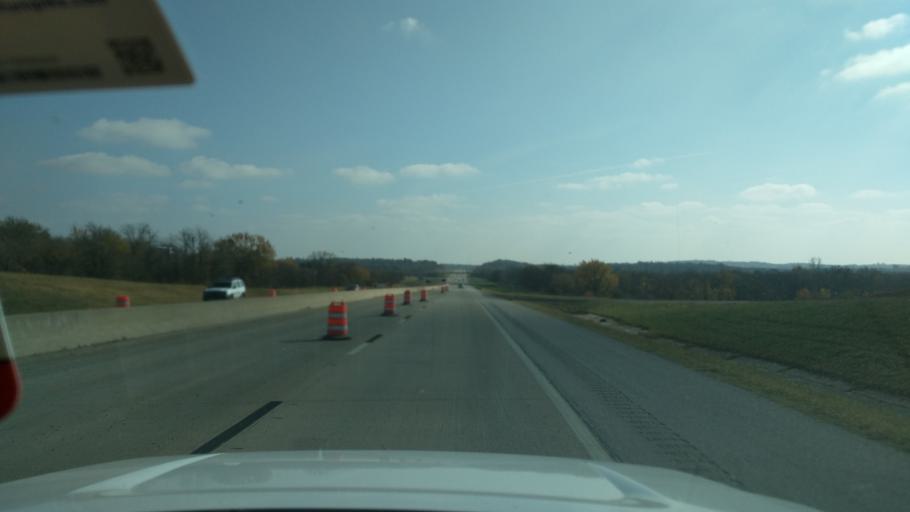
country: US
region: Oklahoma
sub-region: Wagoner County
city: Coweta
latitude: 36.0124
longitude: -95.6661
